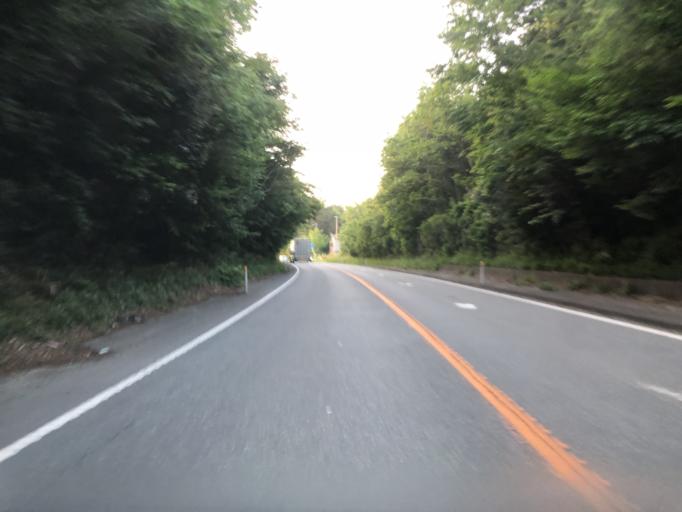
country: JP
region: Fukushima
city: Namie
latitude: 37.3924
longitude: 141.0067
